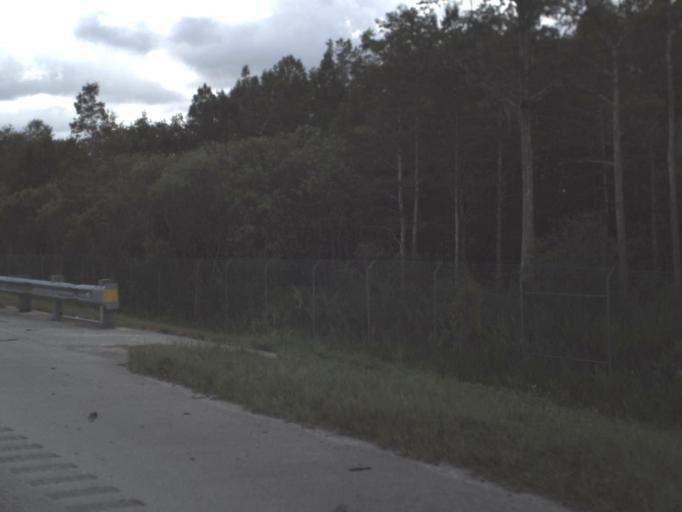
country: US
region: Florida
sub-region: Collier County
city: Immokalee
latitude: 26.1549
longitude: -81.3120
